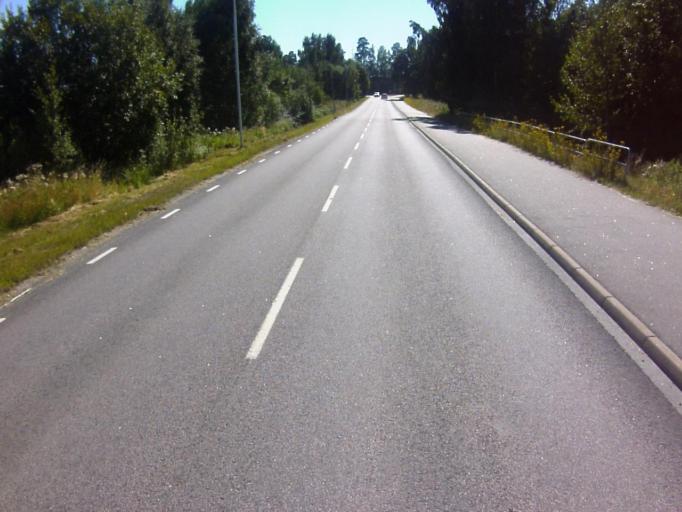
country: SE
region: Soedermanland
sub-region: Eskilstuna Kommun
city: Hallbybrunn
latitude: 59.3821
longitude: 16.4347
